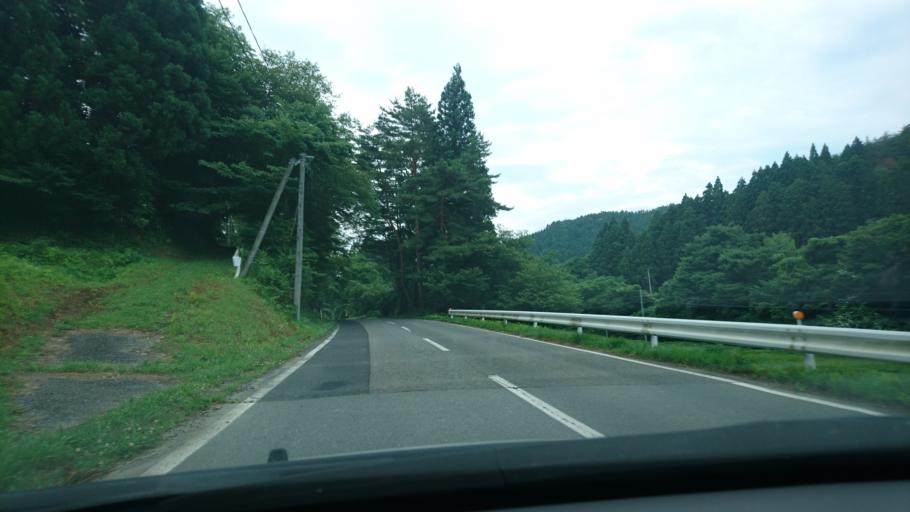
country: JP
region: Iwate
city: Ichinoseki
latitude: 38.8759
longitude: 141.4261
